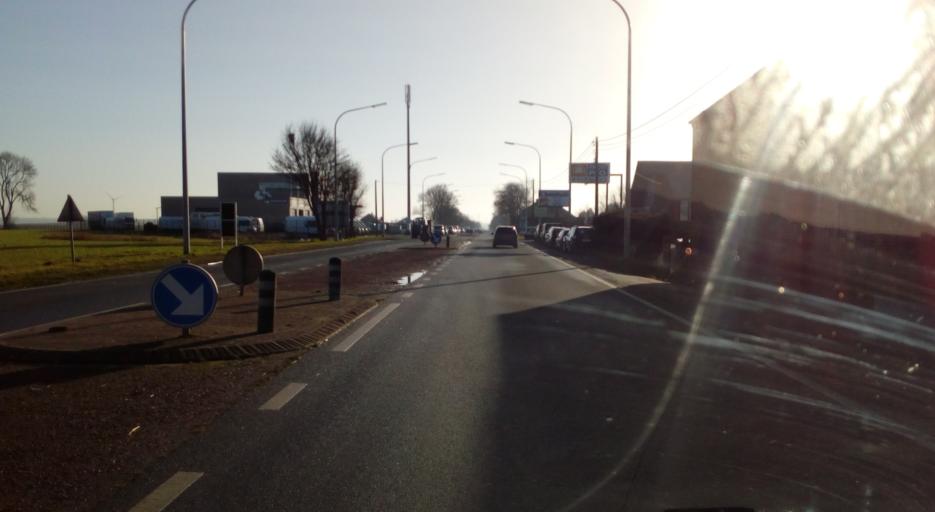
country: BE
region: Wallonia
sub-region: Province du Hainaut
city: Gerpinnes
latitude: 50.3172
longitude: 4.4784
